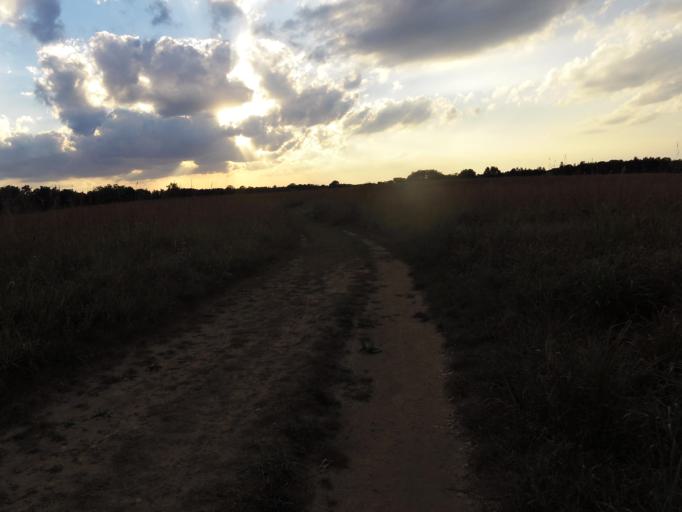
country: US
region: Minnesota
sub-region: Washington County
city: Lake Saint Croix Beach
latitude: 44.9361
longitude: -92.7933
